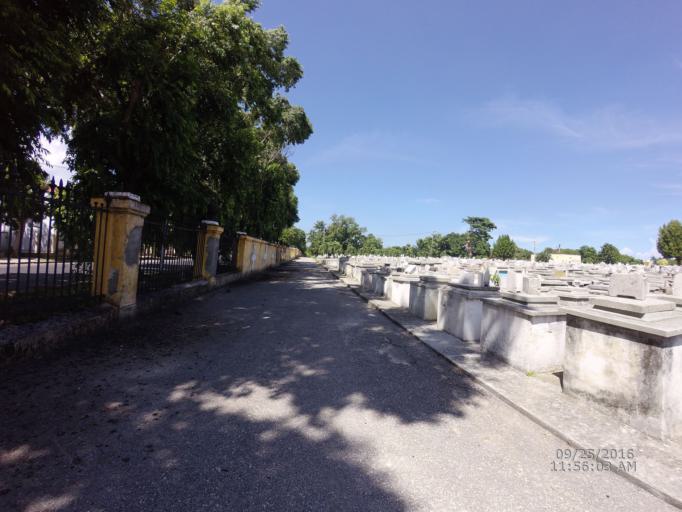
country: CU
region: La Habana
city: Havana
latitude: 23.1200
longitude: -82.3953
